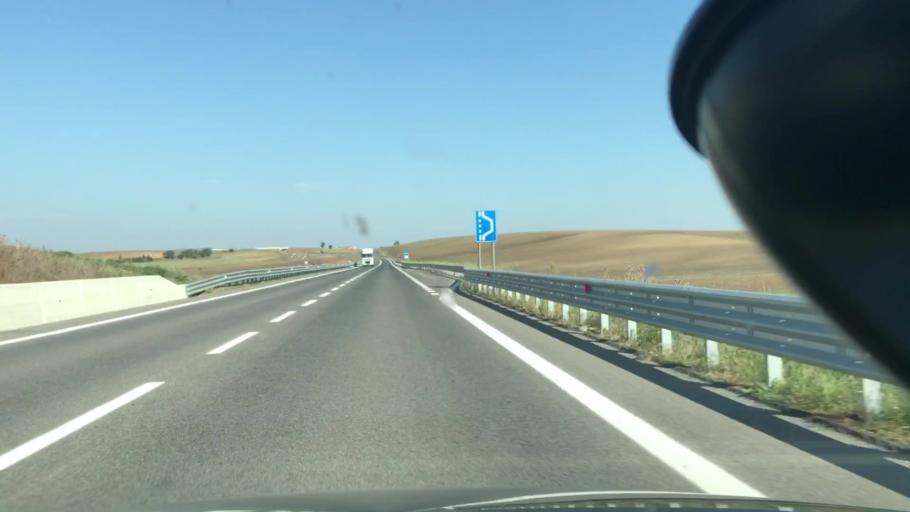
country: IT
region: Basilicate
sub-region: Provincia di Potenza
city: Palazzo San Gervasio
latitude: 40.9600
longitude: 16.0137
